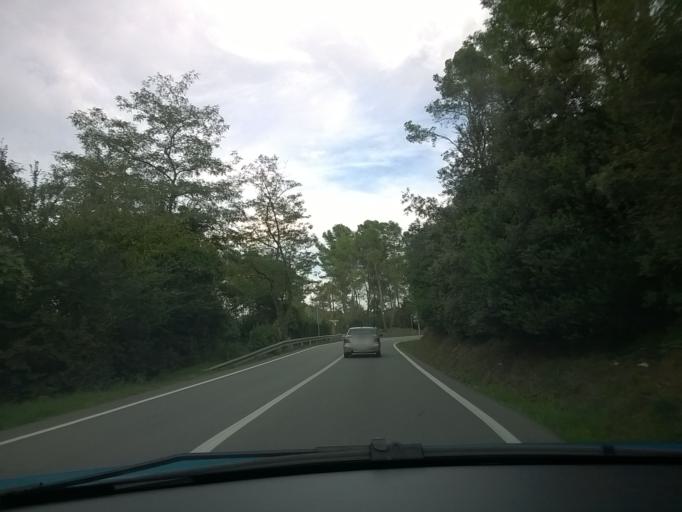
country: ES
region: Catalonia
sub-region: Provincia de Barcelona
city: Sant Cugat del Valles
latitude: 41.4572
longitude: 2.0908
